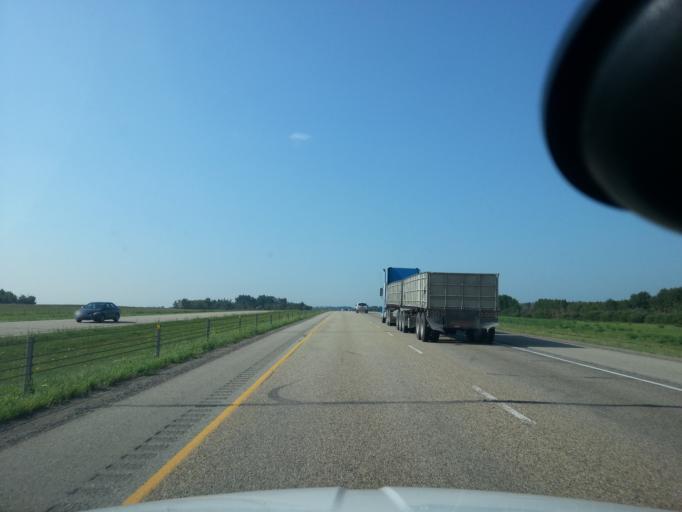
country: CA
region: Alberta
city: Olds
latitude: 51.9676
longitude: -114.0057
